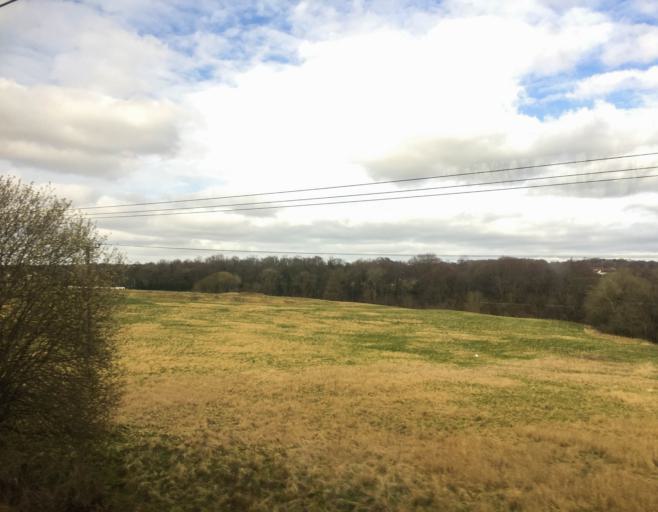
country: GB
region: Scotland
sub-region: North Lanarkshire
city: Newarthill
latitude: 55.7979
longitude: -3.9524
